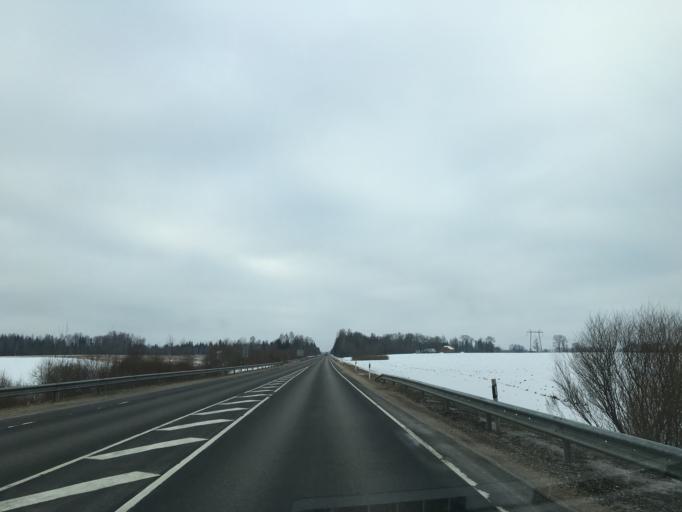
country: EE
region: Tartu
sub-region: Elva linn
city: Elva
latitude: 58.2167
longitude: 26.3654
